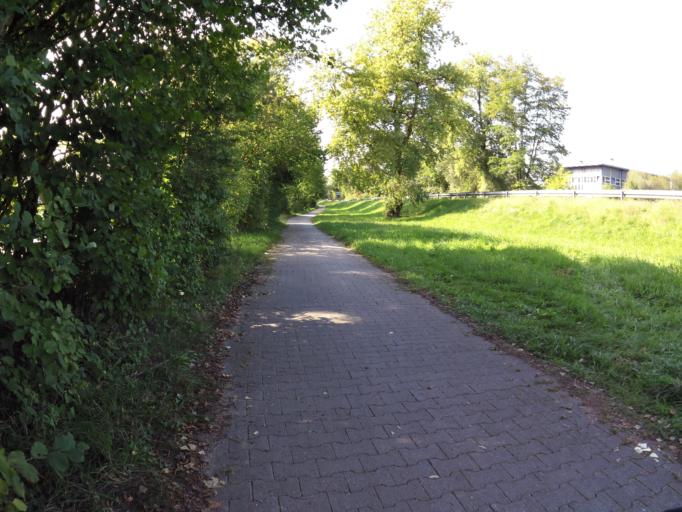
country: DE
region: Baden-Wuerttemberg
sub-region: Freiburg Region
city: Bad Sackingen
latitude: 47.5468
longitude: 7.9366
